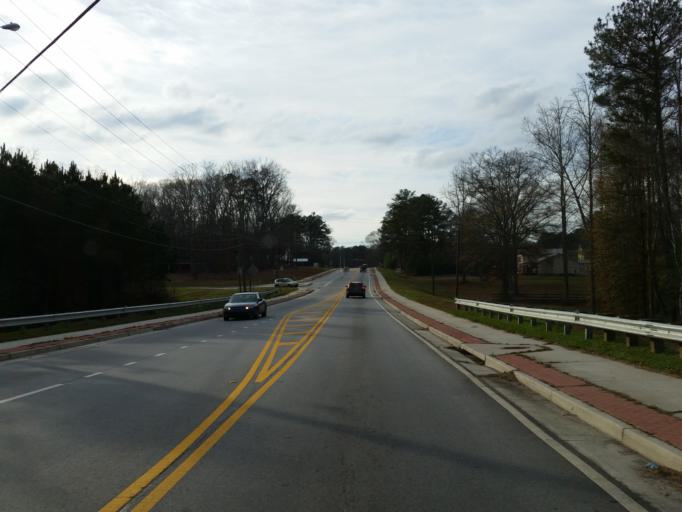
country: US
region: Georgia
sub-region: Cobb County
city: Powder Springs
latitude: 33.9028
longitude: -84.7010
